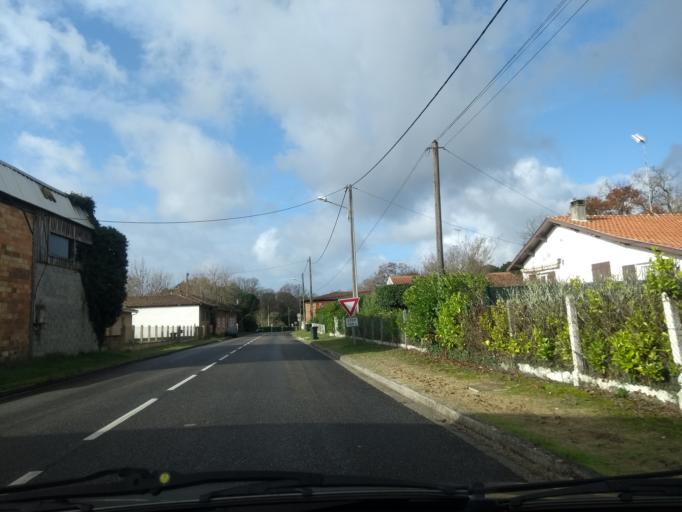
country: FR
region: Aquitaine
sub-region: Departement de la Gironde
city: Belin-Beliet
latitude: 44.4888
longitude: -0.7897
